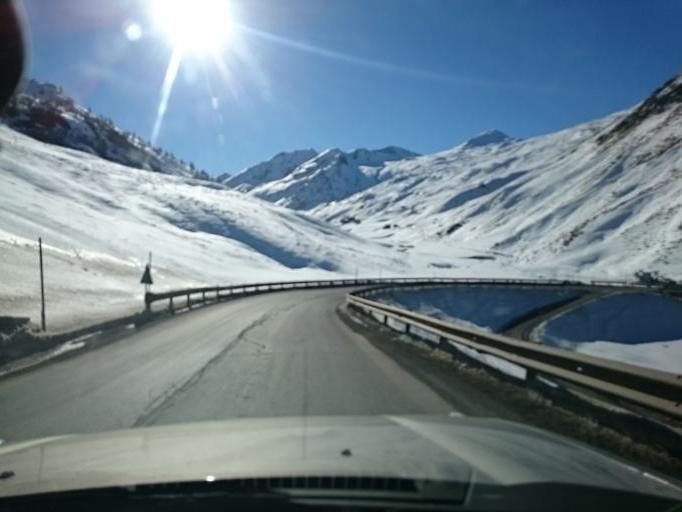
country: IT
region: Lombardy
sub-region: Provincia di Sondrio
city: Livigno
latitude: 46.5166
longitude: 10.1812
